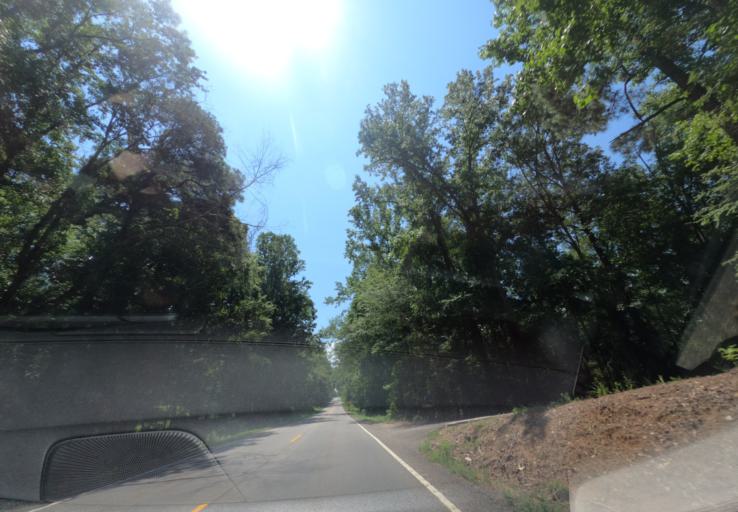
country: US
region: South Carolina
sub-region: Edgefield County
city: Murphys Estates
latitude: 33.5689
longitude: -82.0135
